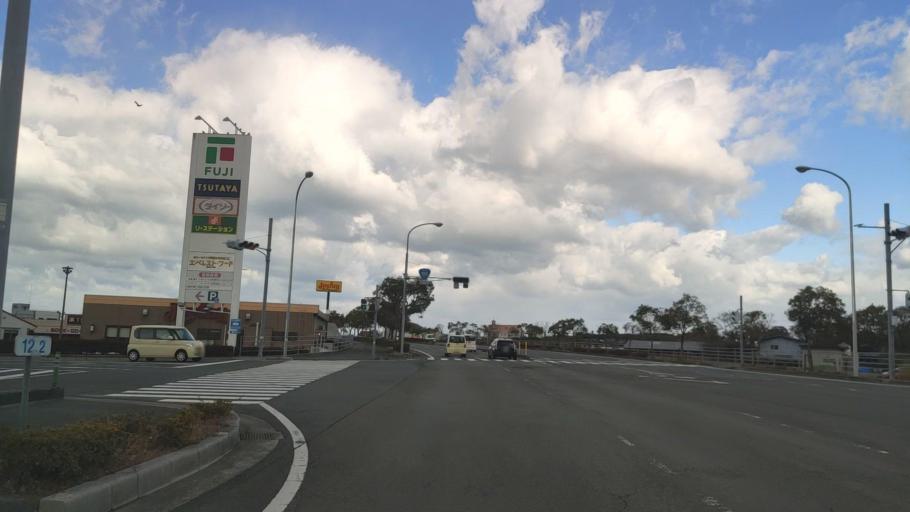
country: JP
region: Ehime
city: Hojo
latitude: 33.9455
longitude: 132.7760
